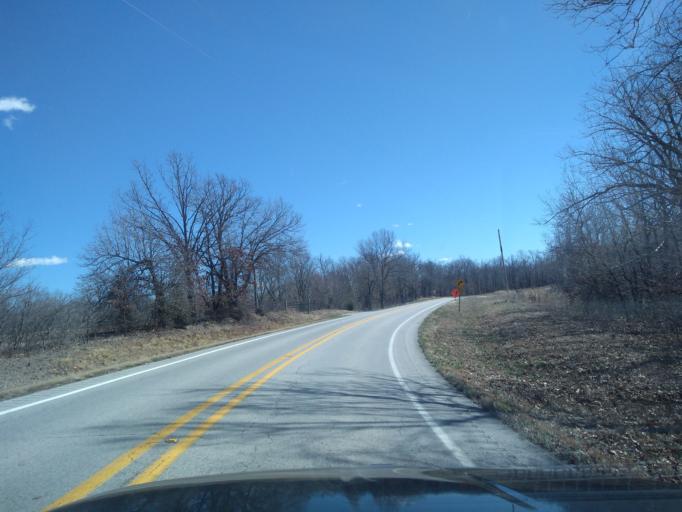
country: US
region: Arkansas
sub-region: Washington County
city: Farmington
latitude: 36.0882
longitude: -94.3279
